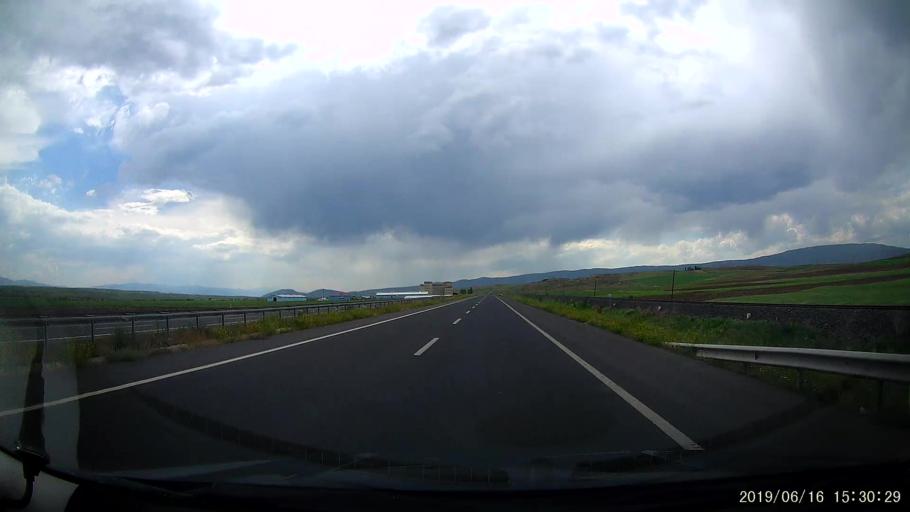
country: TR
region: Erzurum
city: Horasan
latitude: 40.0338
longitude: 42.1040
